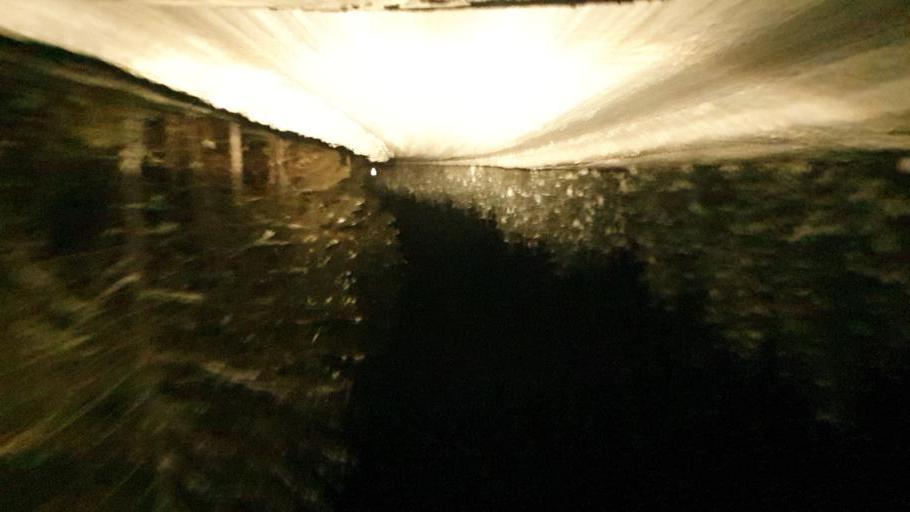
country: EE
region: Vorumaa
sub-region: Antsla vald
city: Vana-Antsla
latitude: 57.9498
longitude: 26.6377
